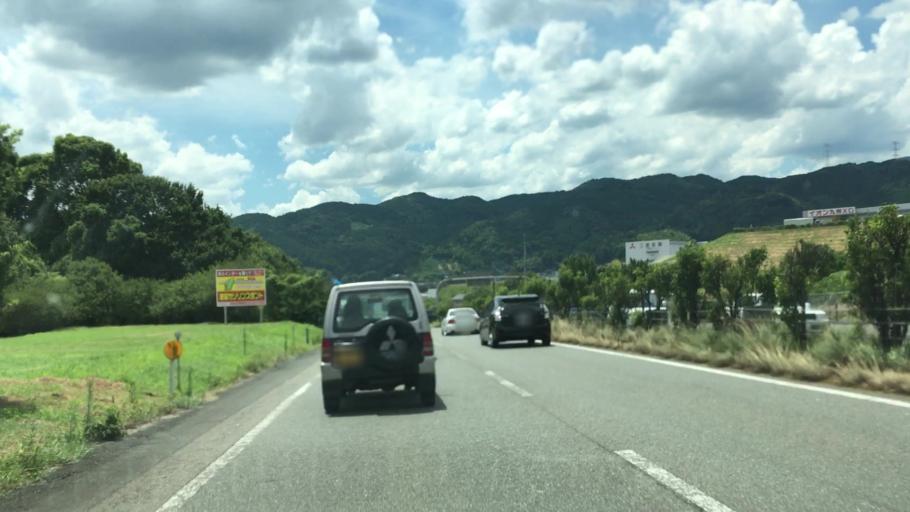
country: JP
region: Saga Prefecture
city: Tosu
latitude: 33.4240
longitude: 130.5144
